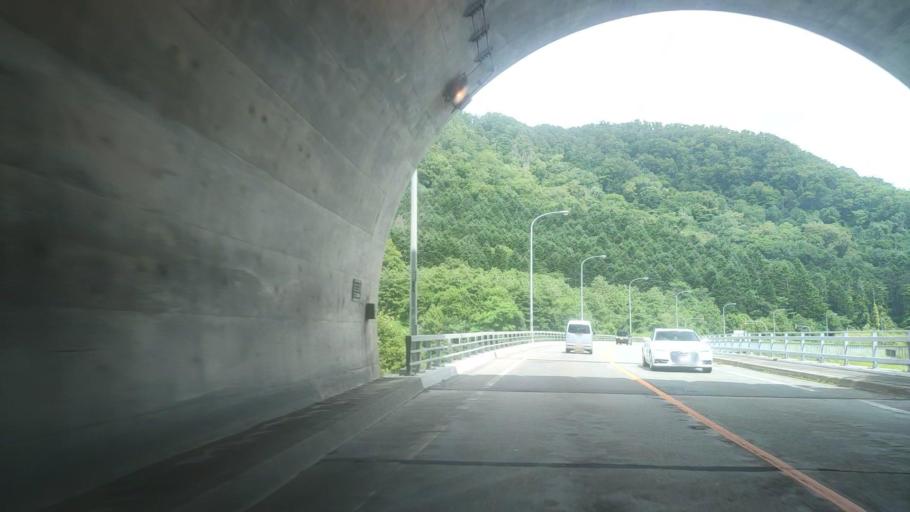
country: JP
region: Hokkaido
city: Niseko Town
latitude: 42.6033
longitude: 140.5595
